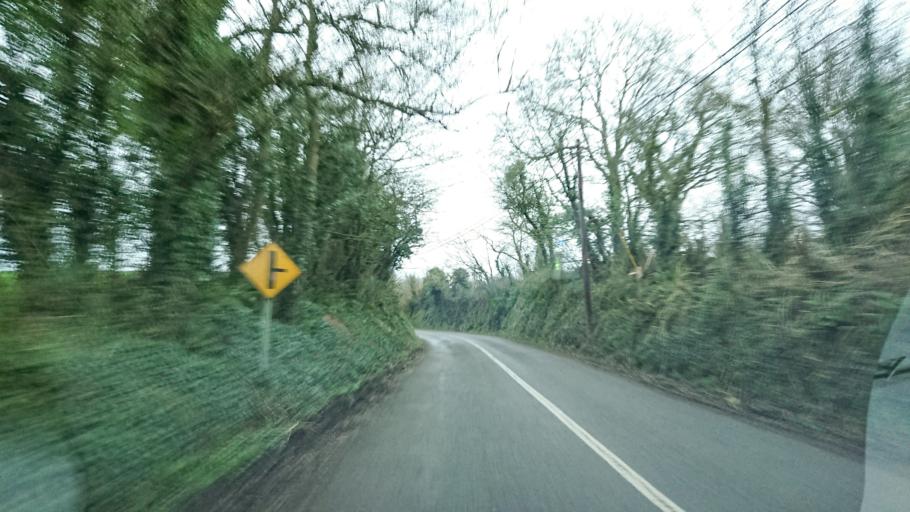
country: IE
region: Munster
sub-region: Waterford
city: Portlaw
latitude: 52.1745
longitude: -7.4043
